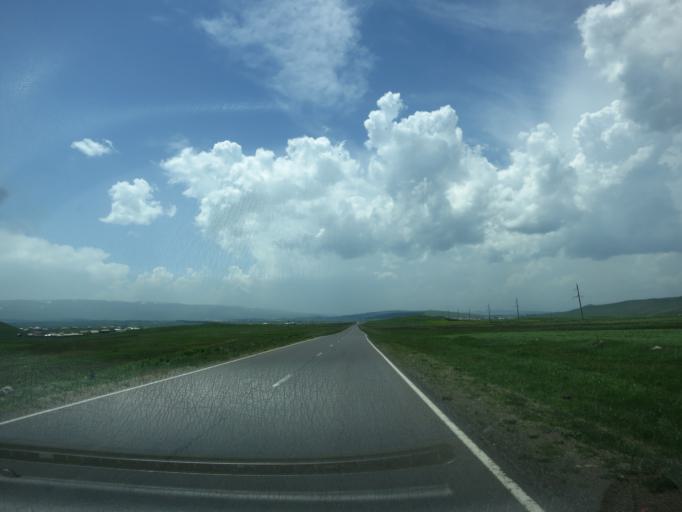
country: GE
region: Samtskhe-Javakheti
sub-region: Ninotsminda
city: Ninotsminda
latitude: 41.2964
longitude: 43.6688
